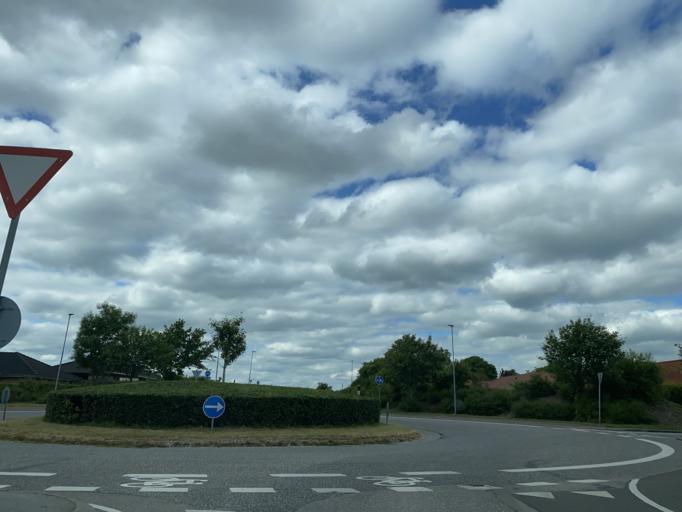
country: DK
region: Central Jutland
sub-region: Arhus Kommune
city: Framlev
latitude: 56.1471
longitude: 9.9870
